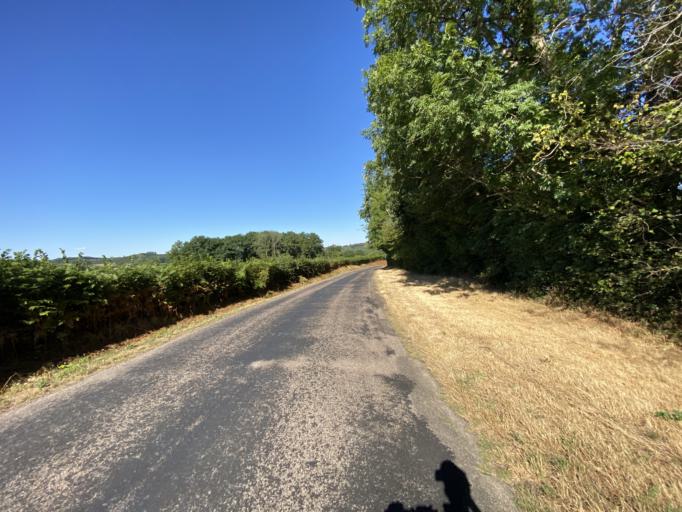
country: FR
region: Bourgogne
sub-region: Departement de la Cote-d'Or
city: Saulieu
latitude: 47.2753
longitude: 4.1872
